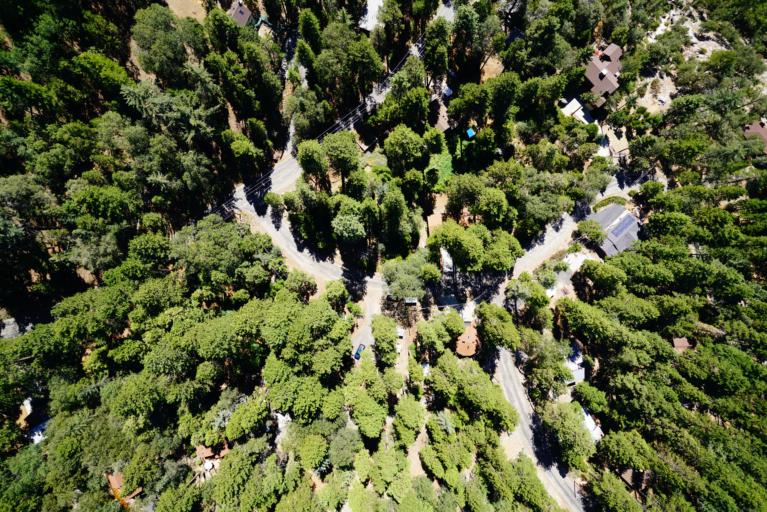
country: US
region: California
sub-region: Riverside County
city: Idyllwild-Pine Cove
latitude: 33.7573
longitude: -116.7470
